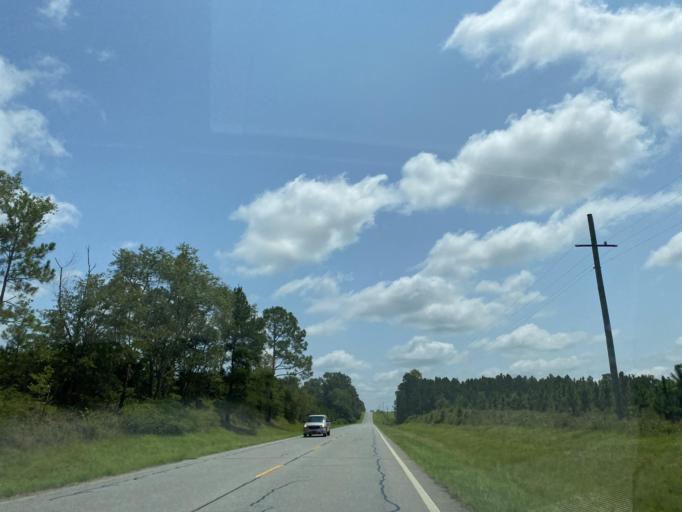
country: US
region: Georgia
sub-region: Wilcox County
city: Abbeville
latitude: 32.0102
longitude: -83.1077
